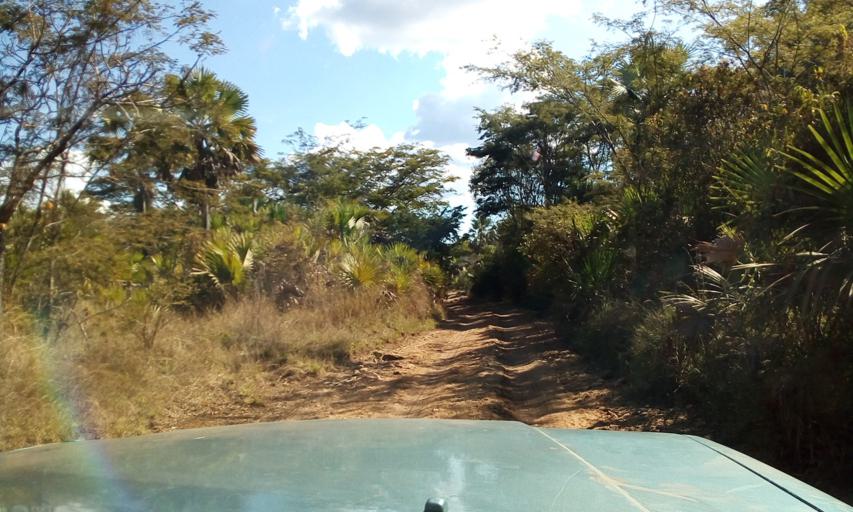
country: MG
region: Boeny
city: Mahajanga
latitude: -16.0587
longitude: 45.8020
